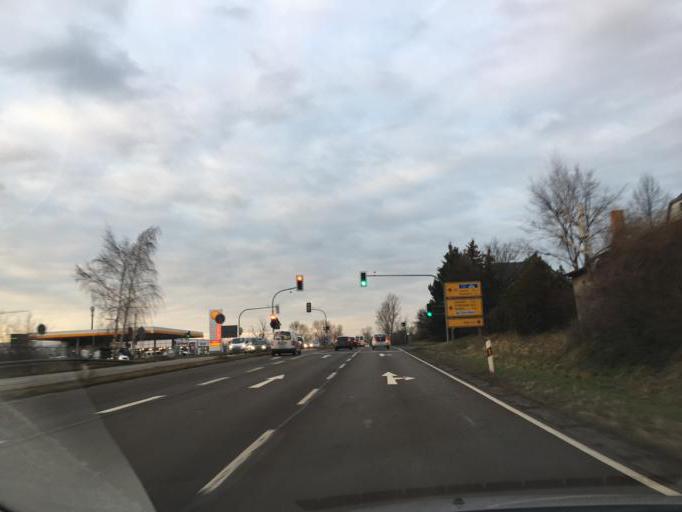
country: DE
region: Saxony
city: Borna
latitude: 51.1512
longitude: 12.5094
